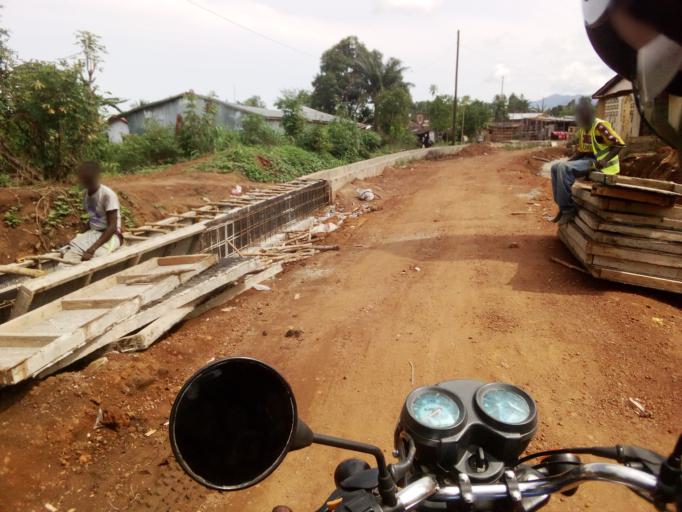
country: SL
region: Western Area
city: Waterloo
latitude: 8.3361
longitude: -13.0725
